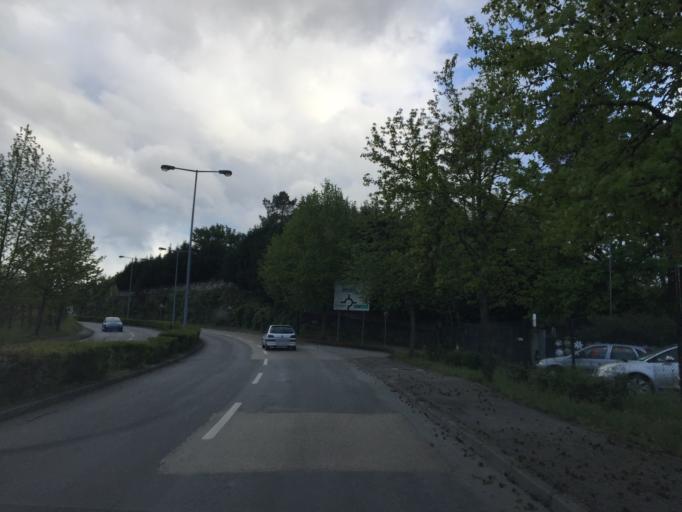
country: PT
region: Viseu
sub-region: Viseu
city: Viseu
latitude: 40.6620
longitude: -7.9240
